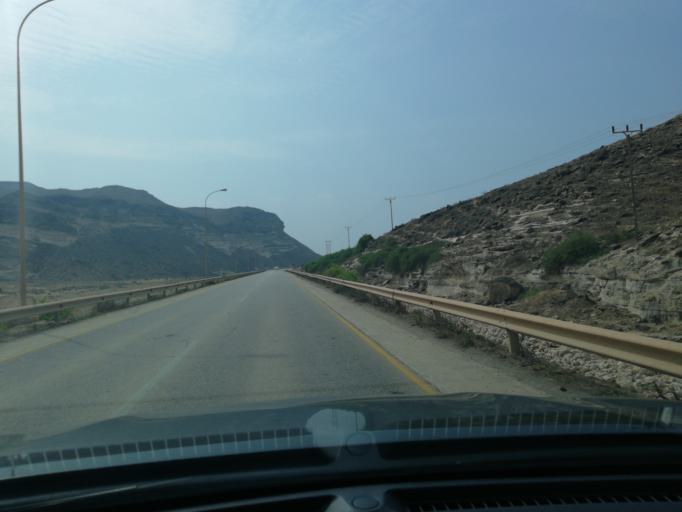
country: OM
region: Zufar
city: Salalah
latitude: 16.8929
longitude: 53.8193
